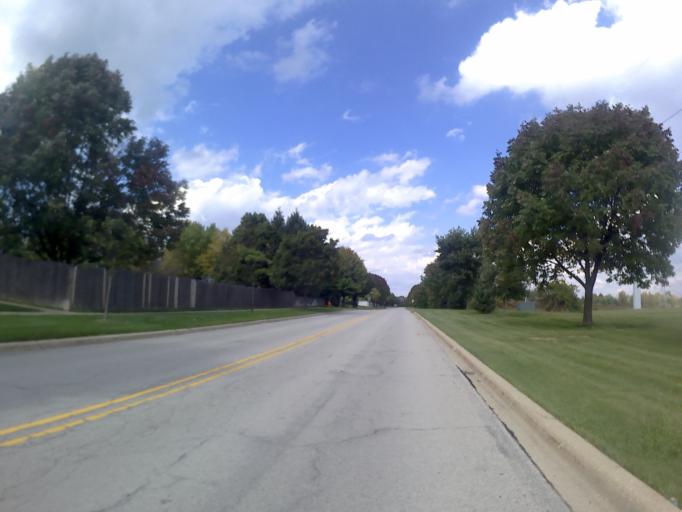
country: US
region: Illinois
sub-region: Will County
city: Bolingbrook
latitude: 41.7307
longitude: -88.0983
